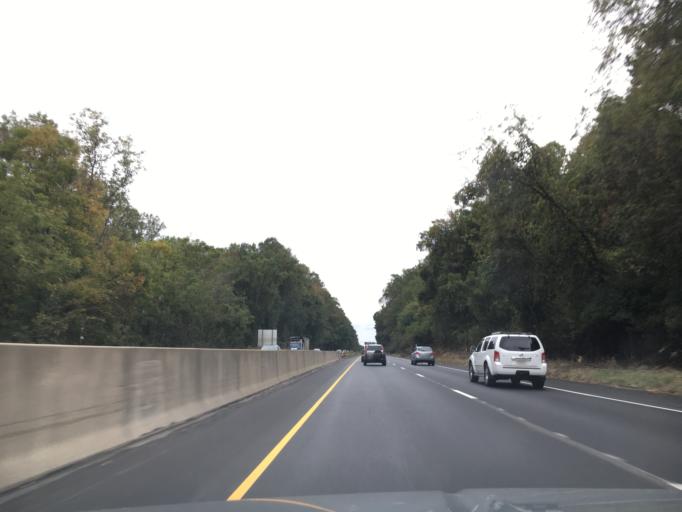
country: US
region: Pennsylvania
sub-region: Chester County
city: Thorndale
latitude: 40.0072
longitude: -75.7515
